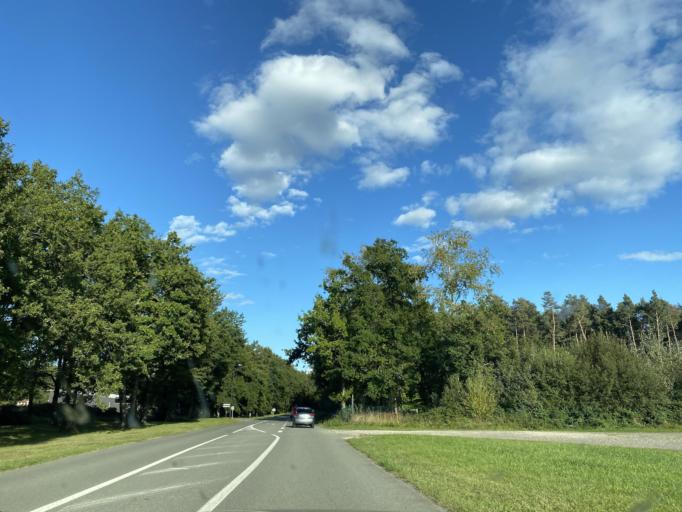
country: FR
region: Auvergne
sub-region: Departement du Puy-de-Dome
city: Randan
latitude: 46.0178
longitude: 3.3828
